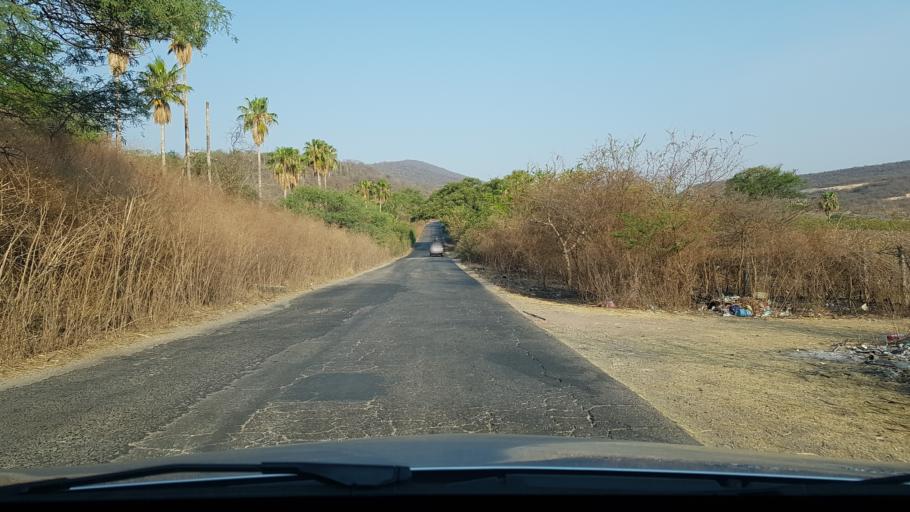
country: MX
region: Morelos
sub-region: Tepalcingo
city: Zacapalco
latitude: 18.6531
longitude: -99.0338
